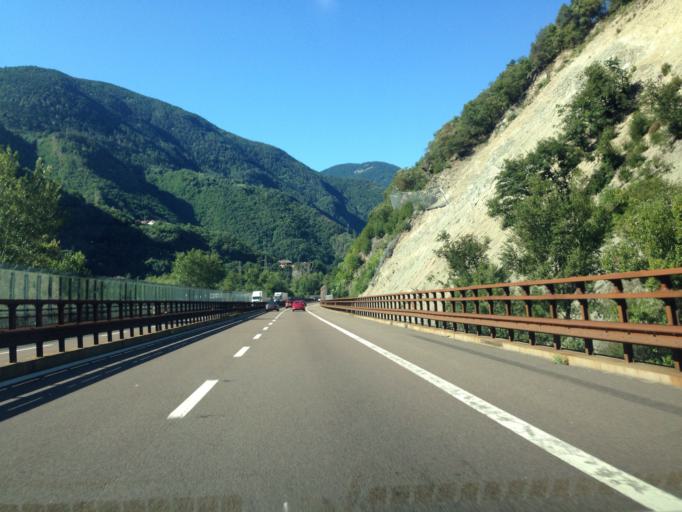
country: IT
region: Trentino-Alto Adige
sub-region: Bolzano
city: Collalbo
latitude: 46.5000
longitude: 11.4518
